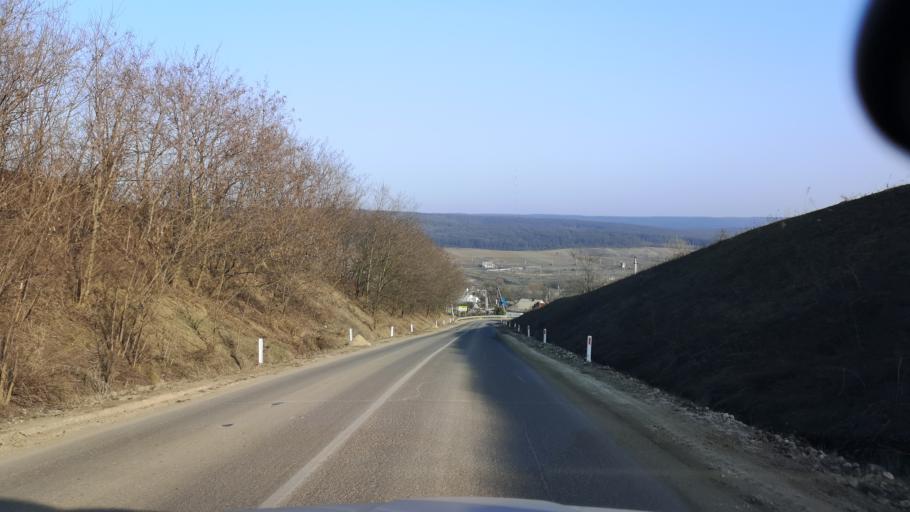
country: MD
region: Stinga Nistrului
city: Bucovat
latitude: 47.1087
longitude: 28.5000
